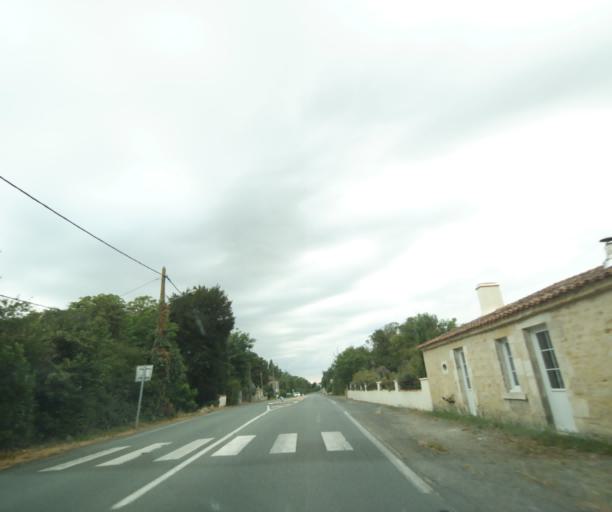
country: FR
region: Pays de la Loire
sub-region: Departement de la Vendee
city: Chaille-les-Marais
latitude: 46.3968
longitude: -1.0278
